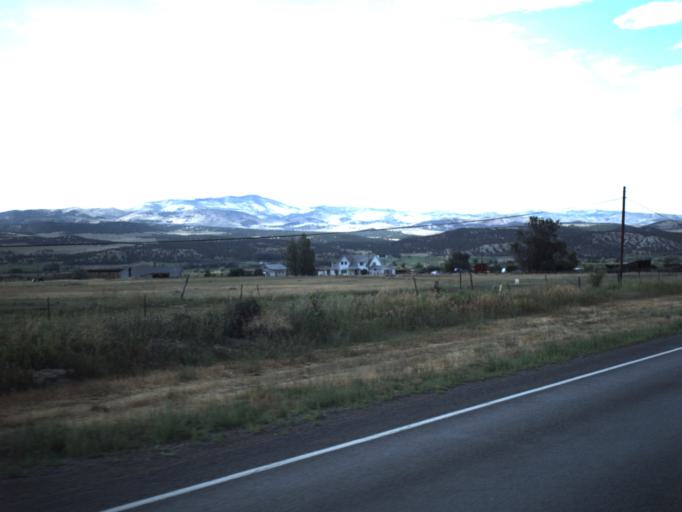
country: US
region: Utah
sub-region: Sanpete County
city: Mount Pleasant
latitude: 39.5594
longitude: -111.4554
